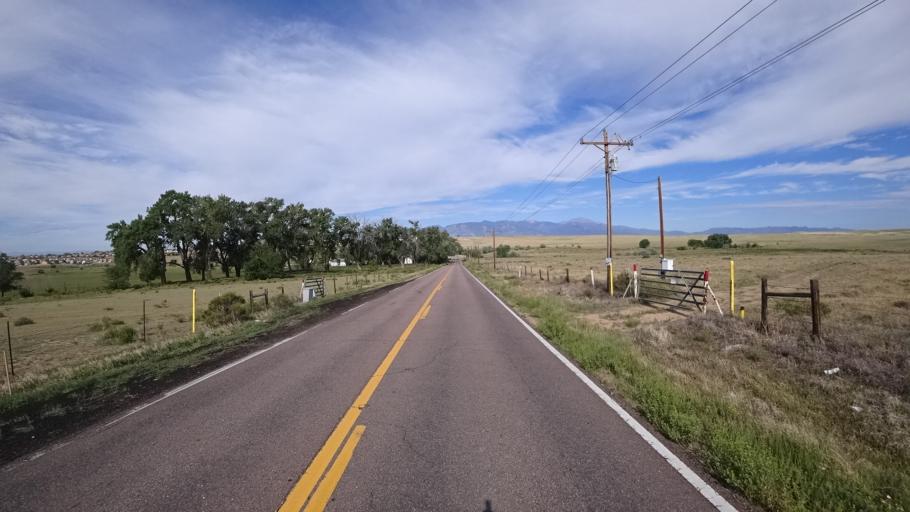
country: US
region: Colorado
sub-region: El Paso County
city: Security-Widefield
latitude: 38.7374
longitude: -104.6621
